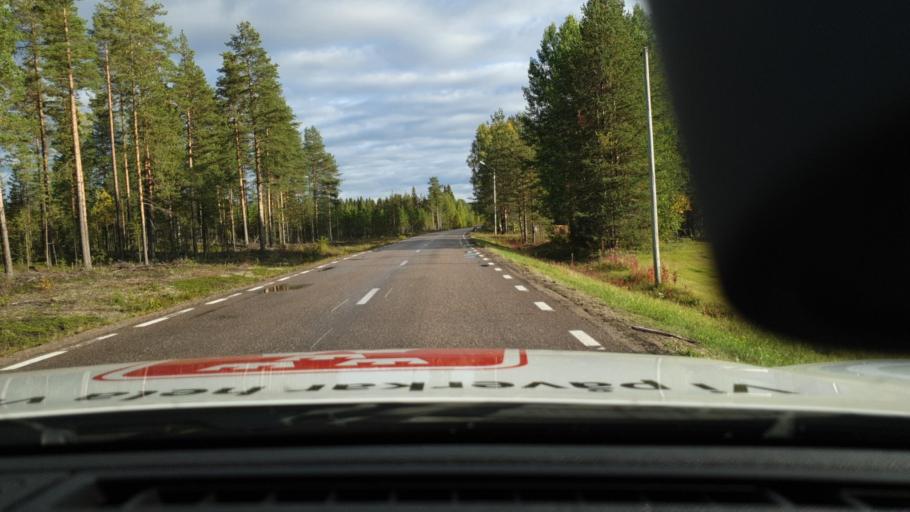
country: SE
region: Norrbotten
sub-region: Overkalix Kommun
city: OEverkalix
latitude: 66.6222
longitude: 22.7441
